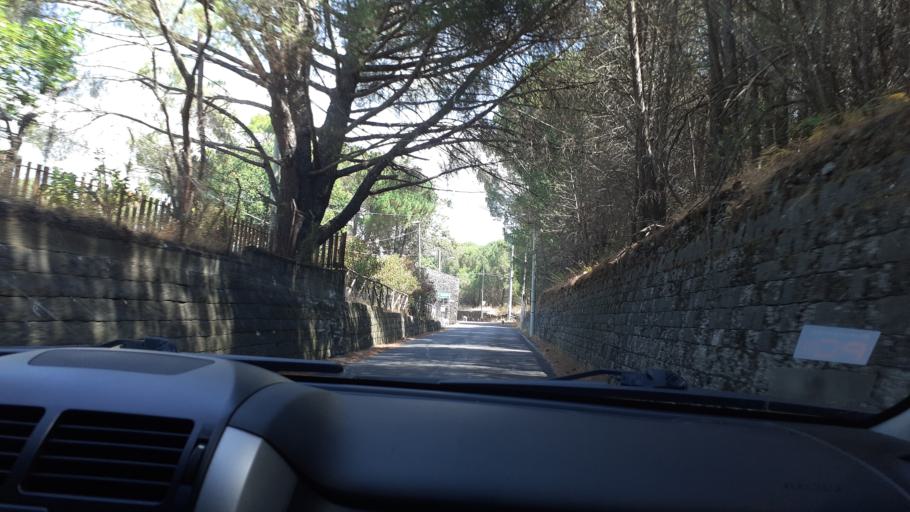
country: IT
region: Sicily
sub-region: Catania
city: Nicolosi
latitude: 37.6298
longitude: 15.0242
